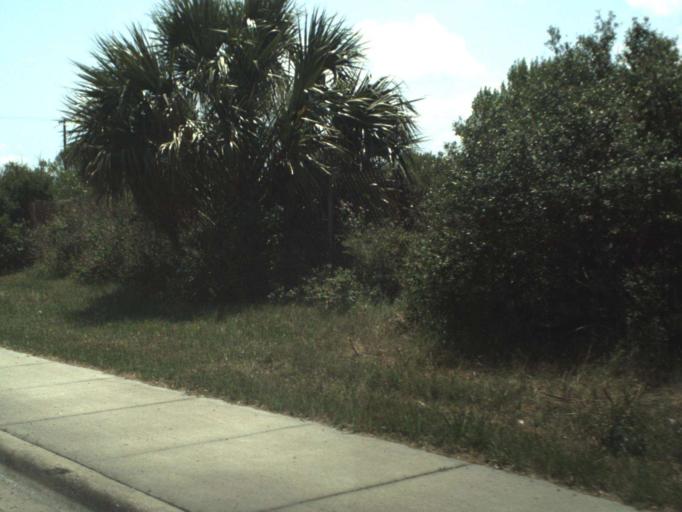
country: US
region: Florida
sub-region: Volusia County
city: New Smyrna Beach
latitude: 29.0198
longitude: -80.9248
